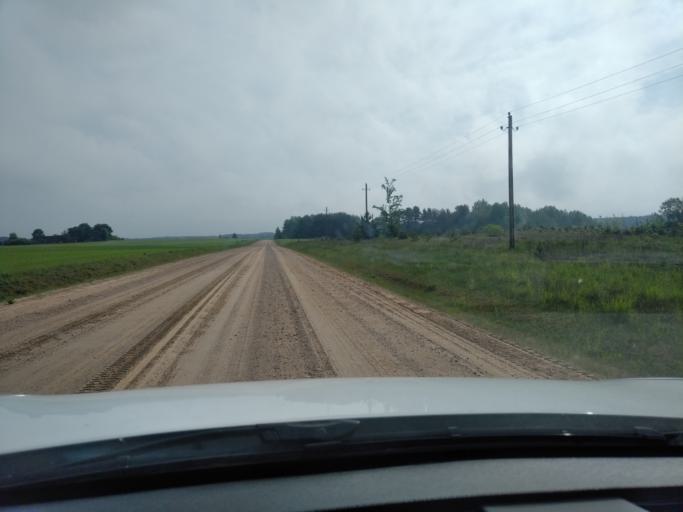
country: LT
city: Svencionys
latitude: 55.2423
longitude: 26.1503
